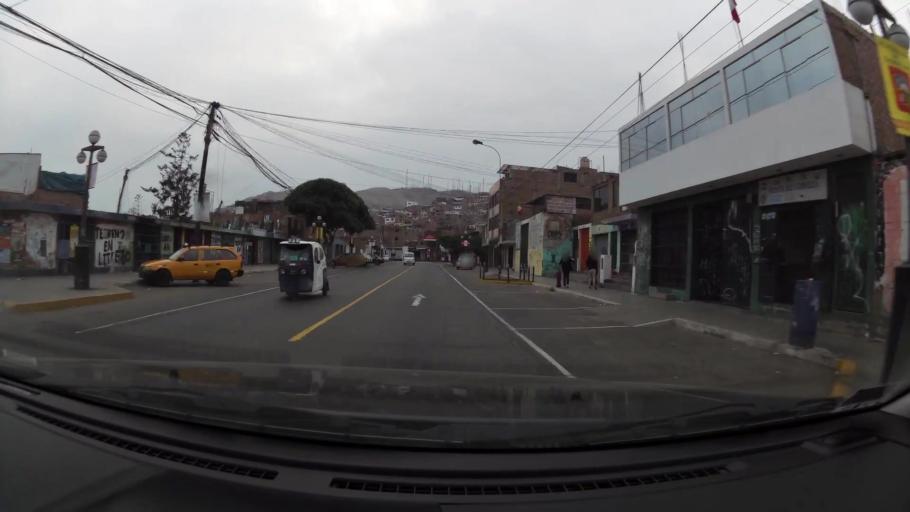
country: PE
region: Lima
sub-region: Lima
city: Surco
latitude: -12.1873
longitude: -77.0097
